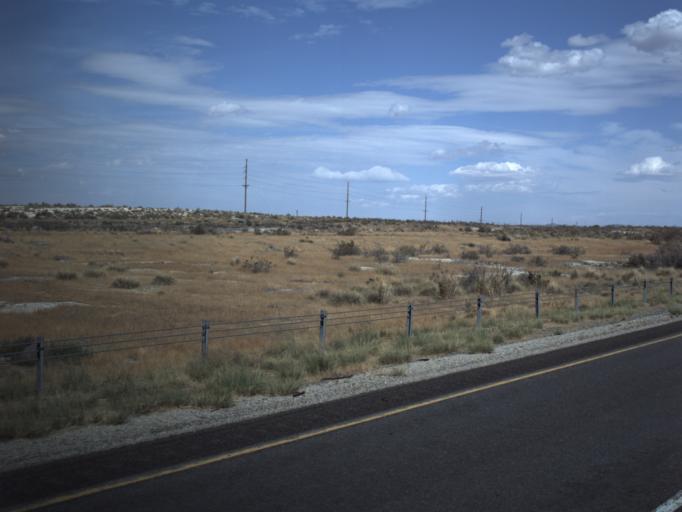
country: US
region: Utah
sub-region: Tooele County
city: Grantsville
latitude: 40.7254
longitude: -113.1381
